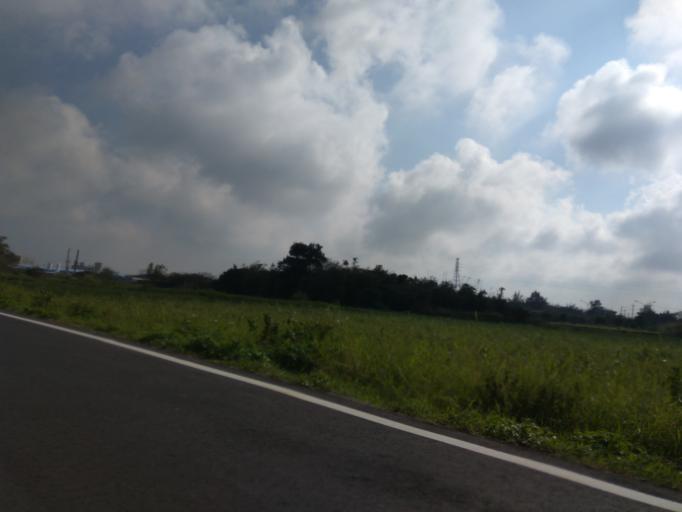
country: TW
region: Taiwan
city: Taoyuan City
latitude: 25.0711
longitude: 121.1741
